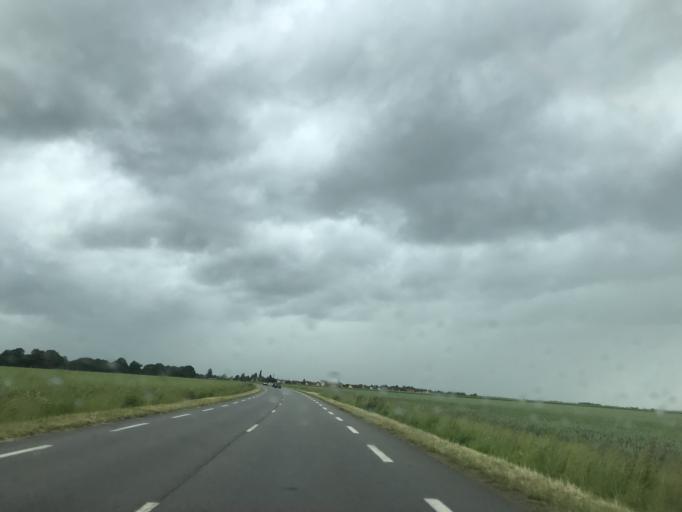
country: FR
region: Haute-Normandie
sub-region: Departement de l'Eure
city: Marcilly-sur-Eure
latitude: 48.9105
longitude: 1.3017
